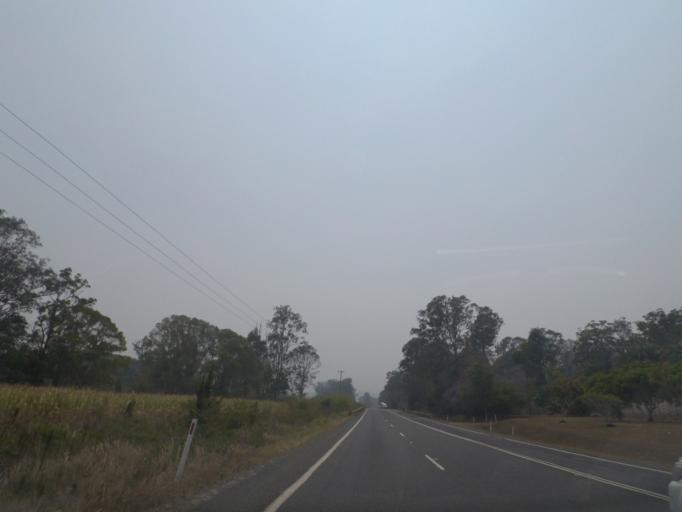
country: AU
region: New South Wales
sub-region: Clarence Valley
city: Maclean
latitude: -29.5595
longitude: 153.1498
